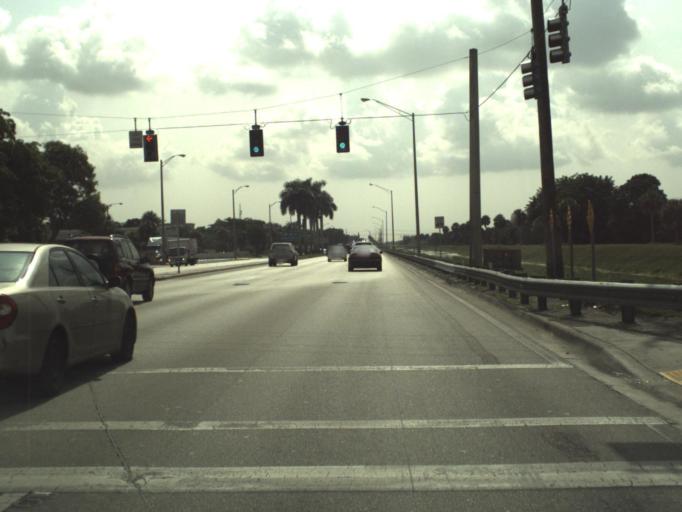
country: US
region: Florida
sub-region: Broward County
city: Plantation
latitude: 26.1357
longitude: -80.2317
